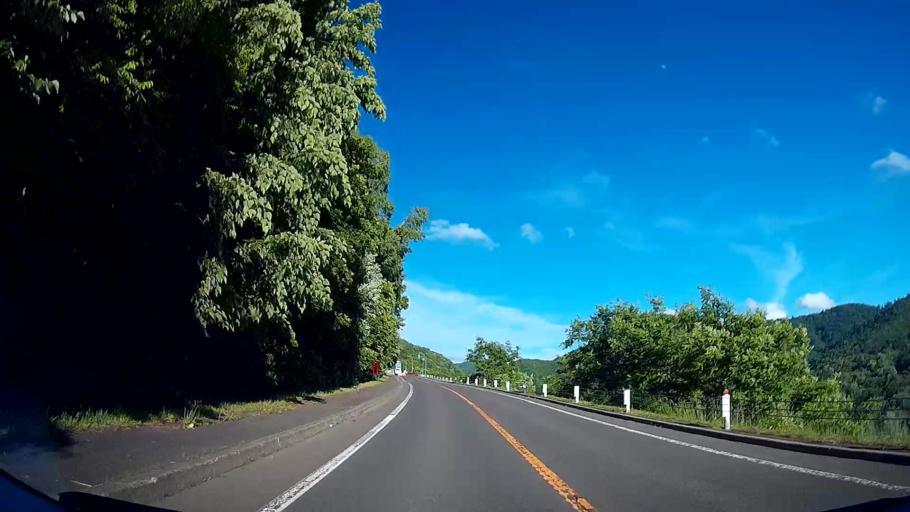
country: JP
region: Hokkaido
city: Sapporo
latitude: 42.9780
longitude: 141.1397
